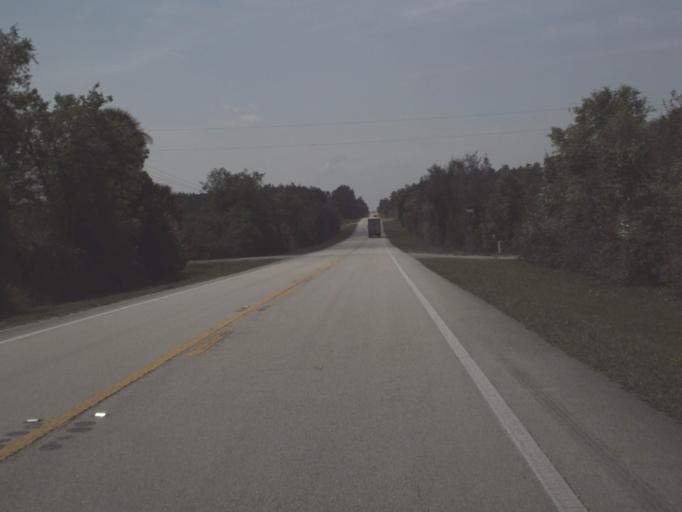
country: US
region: Florida
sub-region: Lake County
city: Astor
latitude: 29.2734
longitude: -81.6467
